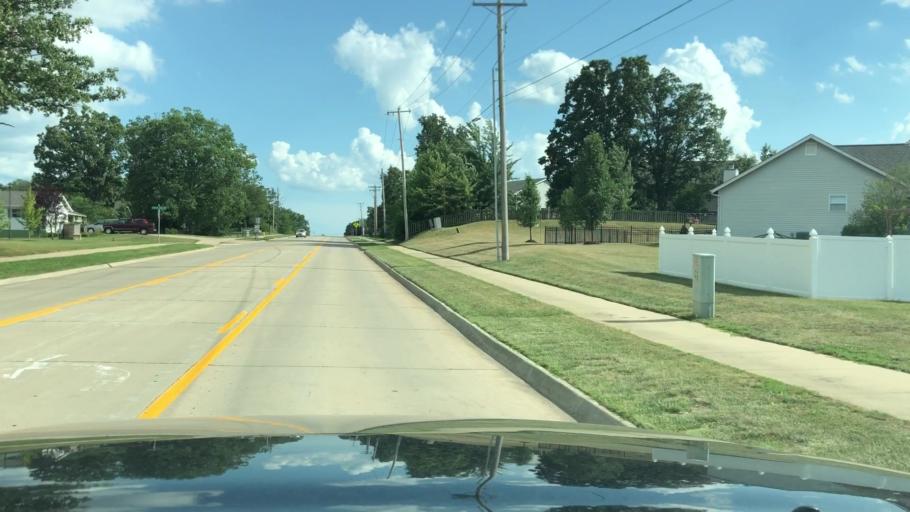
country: US
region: Missouri
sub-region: Saint Charles County
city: Wentzville
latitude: 38.8330
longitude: -90.8922
